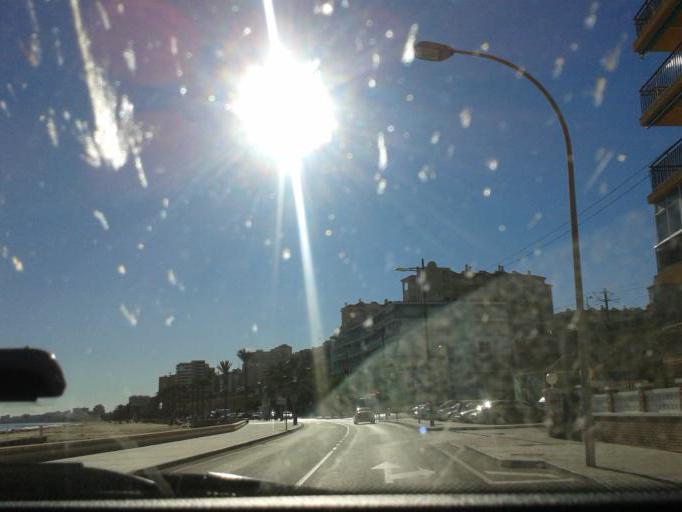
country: ES
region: Valencia
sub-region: Provincia de Alicante
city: el Campello
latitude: 38.4126
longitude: -0.4011
